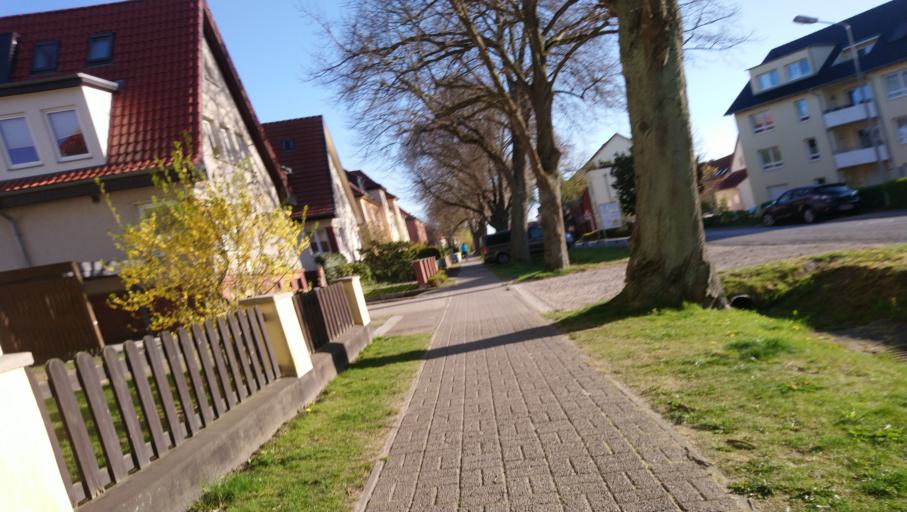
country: DE
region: Mecklenburg-Vorpommern
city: Rostock
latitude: 54.0694
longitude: 12.1351
